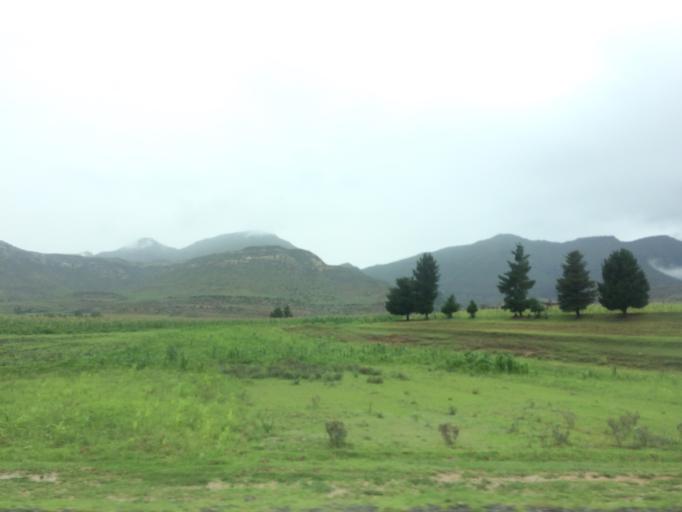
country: LS
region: Maseru
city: Nako
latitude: -29.7682
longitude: 27.5252
